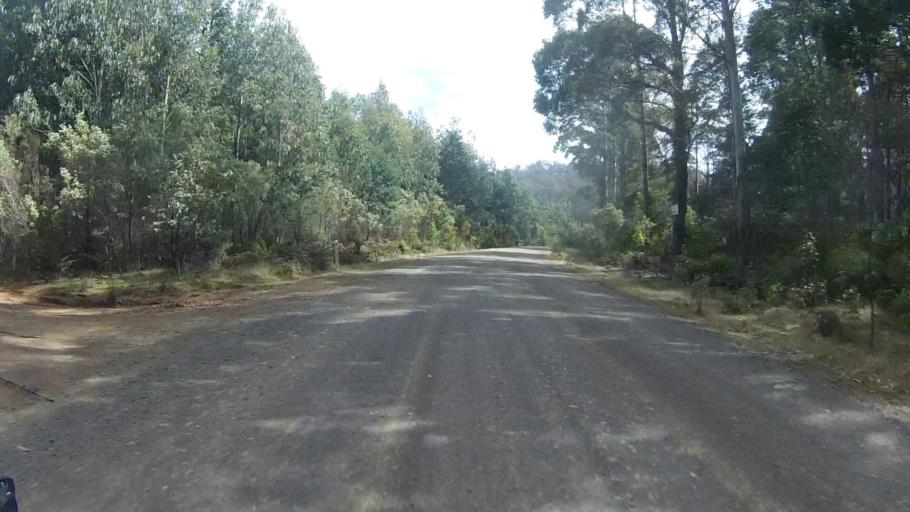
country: AU
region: Tasmania
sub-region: Sorell
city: Sorell
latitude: -42.7438
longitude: 147.8283
